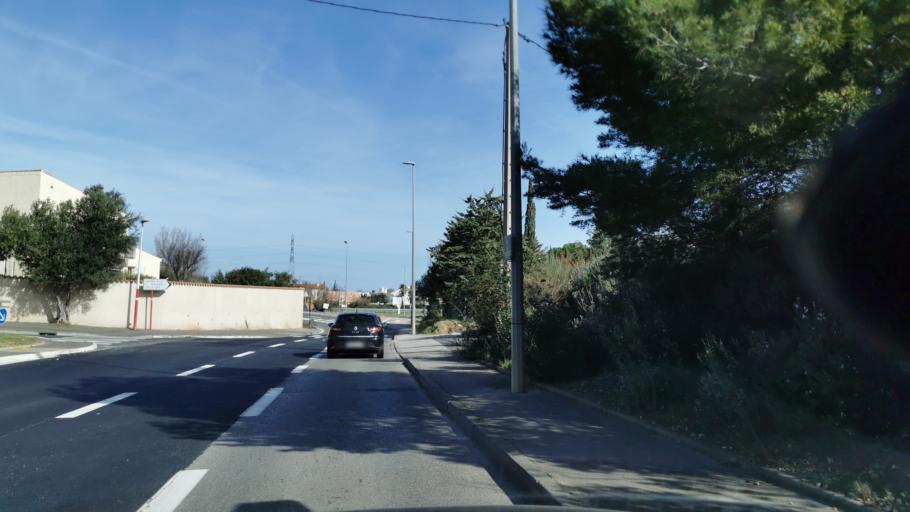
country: FR
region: Languedoc-Roussillon
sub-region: Departement de l'Aude
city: Narbonne
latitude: 43.1662
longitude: 2.9819
